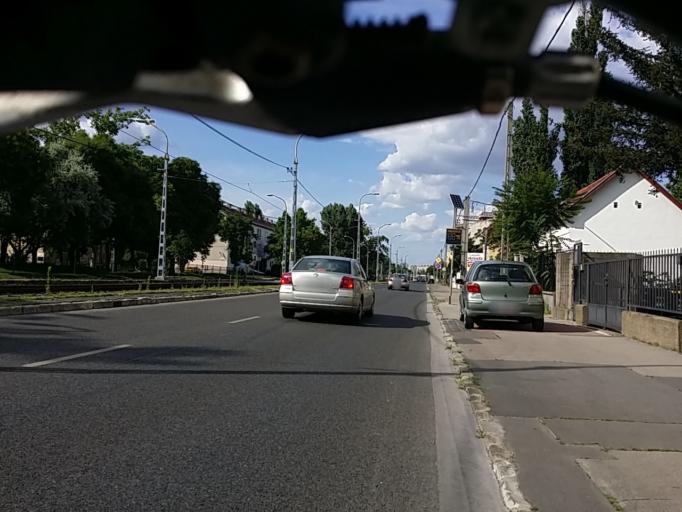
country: HU
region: Budapest
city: Budapest XIII. keruelet
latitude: 47.5435
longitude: 19.0877
